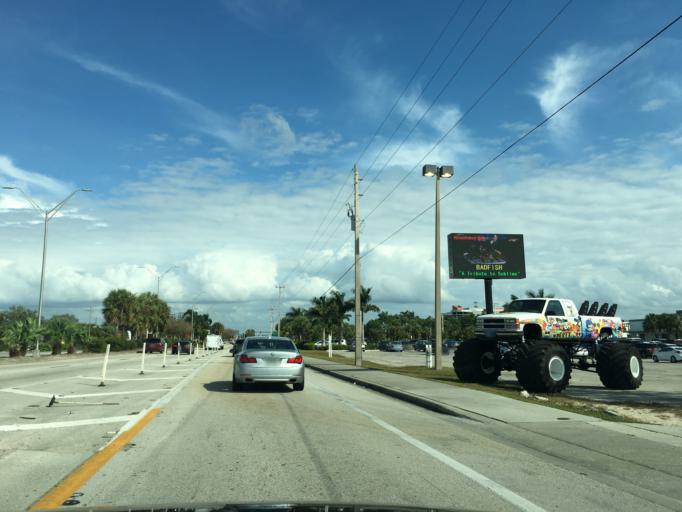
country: US
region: Florida
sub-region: Lee County
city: Pine Manor
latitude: 26.5968
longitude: -81.8695
